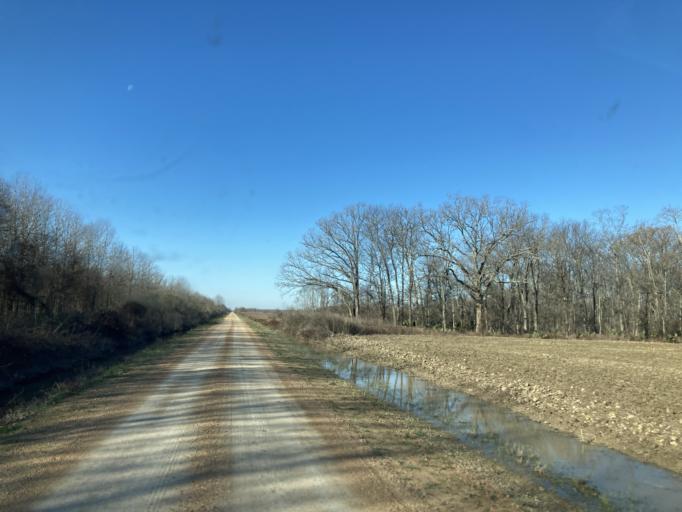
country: US
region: Mississippi
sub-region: Yazoo County
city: Yazoo City
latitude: 32.9519
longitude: -90.6132
